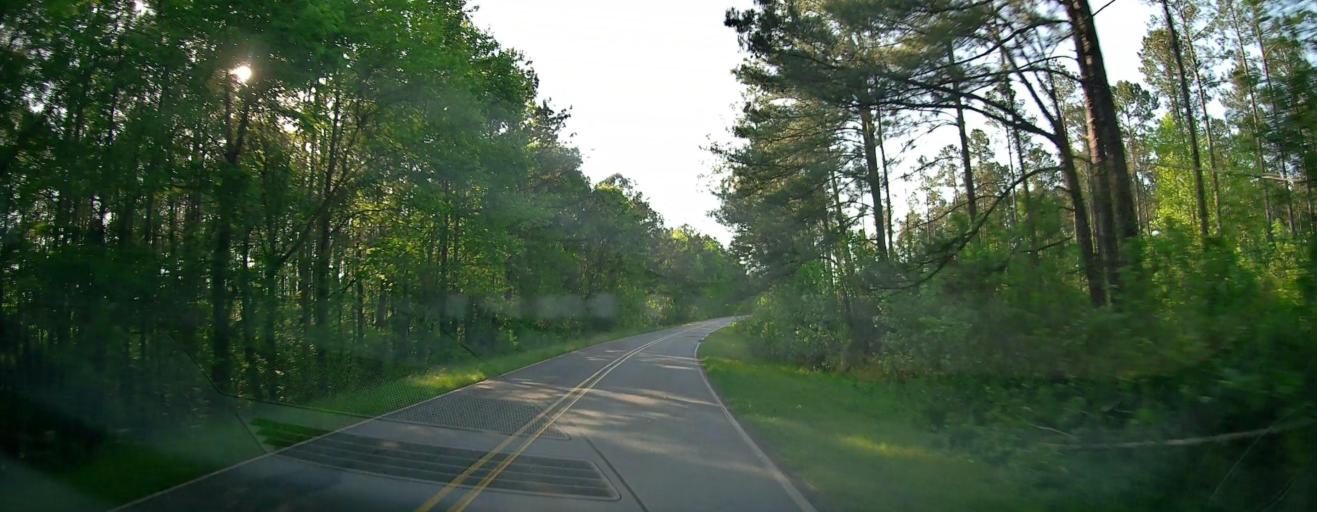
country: US
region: Georgia
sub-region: Putnam County
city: Eatonton
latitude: 33.2740
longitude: -83.3079
